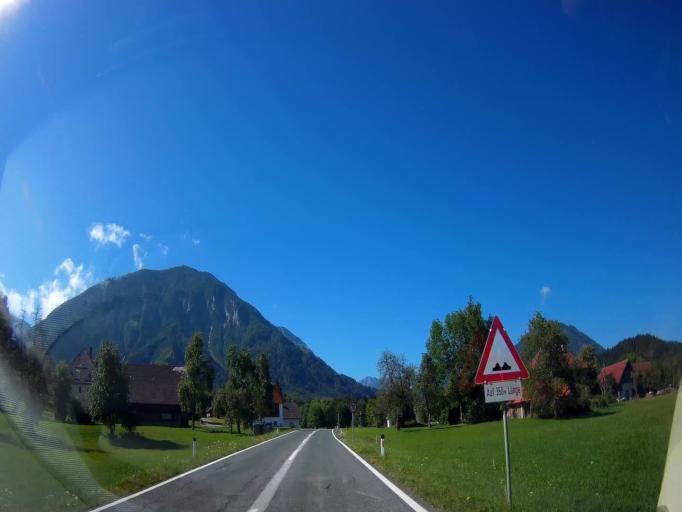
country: AT
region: Carinthia
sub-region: Politischer Bezirk Volkermarkt
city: Gallizien
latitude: 46.5515
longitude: 14.4735
